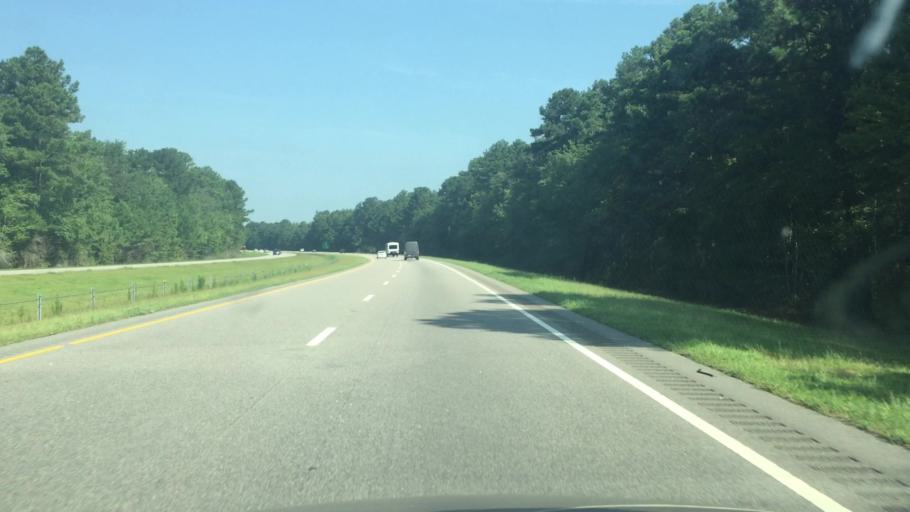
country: US
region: North Carolina
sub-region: Robeson County
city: Lumberton
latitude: 34.5638
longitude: -79.0278
